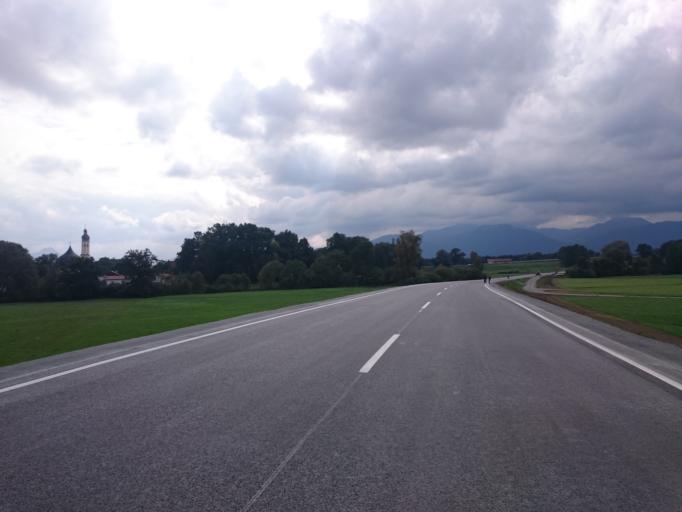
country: DE
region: Bavaria
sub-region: Upper Bavaria
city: Kolbermoor
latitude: 47.8261
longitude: 12.0752
